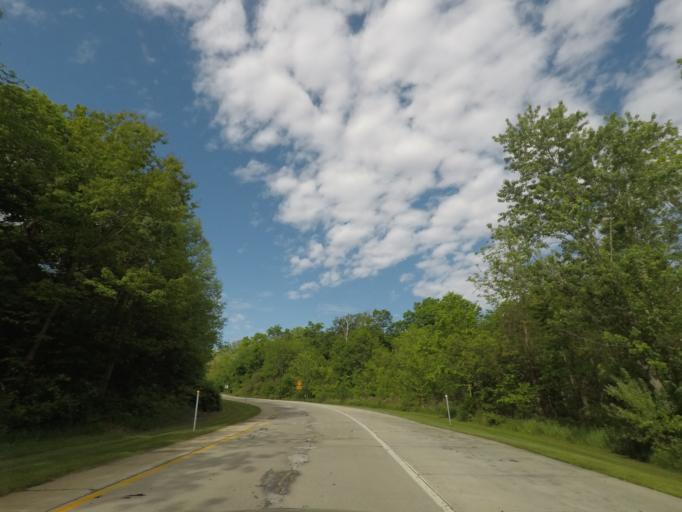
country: US
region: Illinois
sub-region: McLean County
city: Twin Grove
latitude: 40.3617
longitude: -89.1097
